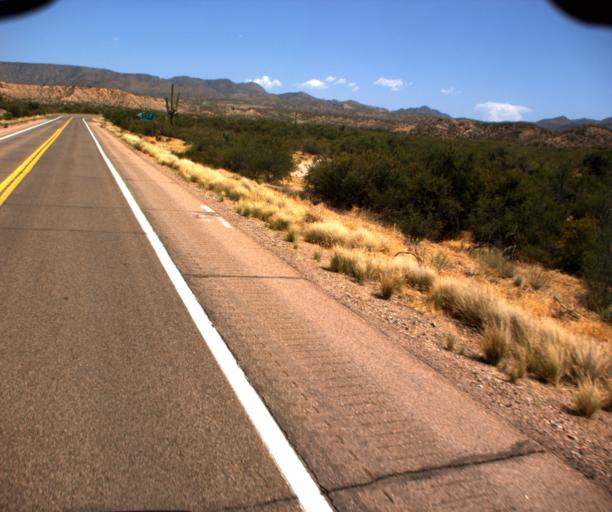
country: US
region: Arizona
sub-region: Gila County
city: Miami
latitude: 33.5955
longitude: -110.9941
